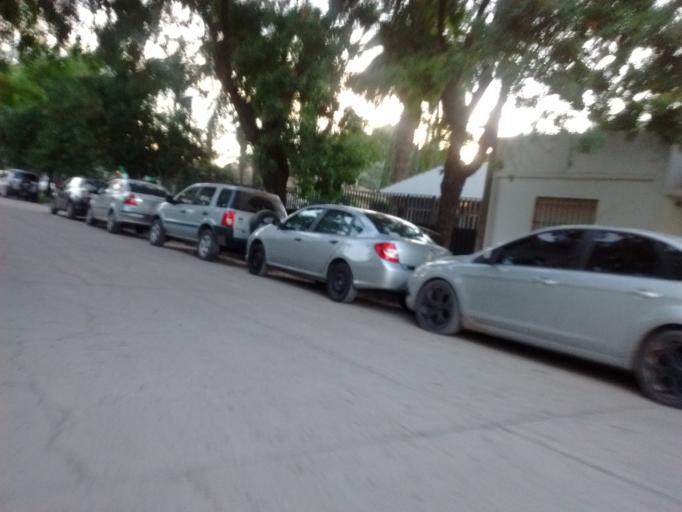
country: AR
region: Santa Fe
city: Funes
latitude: -32.9117
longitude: -60.8149
